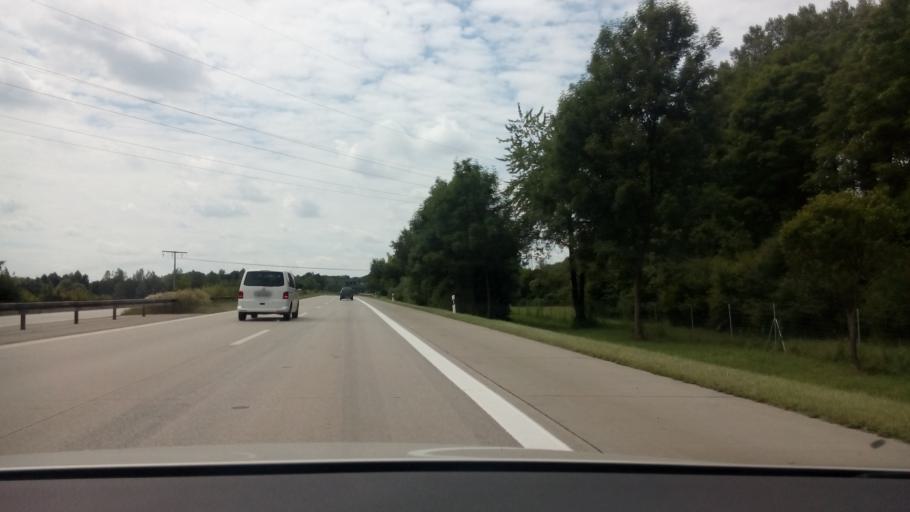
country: DE
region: Bavaria
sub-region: Upper Bavaria
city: Hallbergmoos
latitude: 48.3564
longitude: 11.7315
